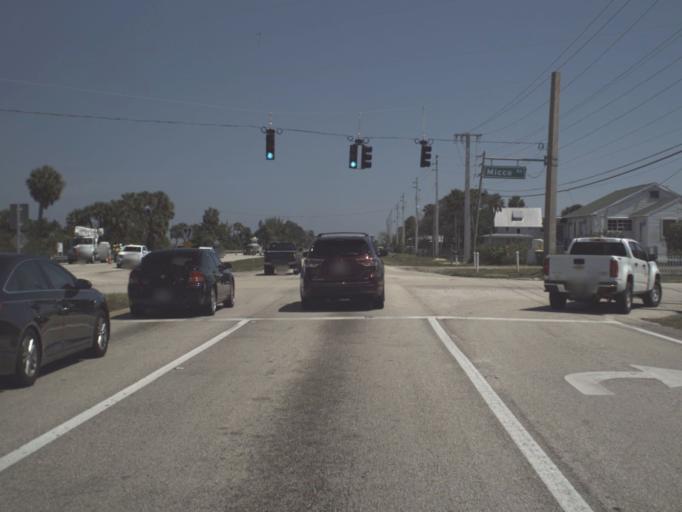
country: US
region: Florida
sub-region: Brevard County
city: Micco
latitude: 27.8807
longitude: -80.5016
